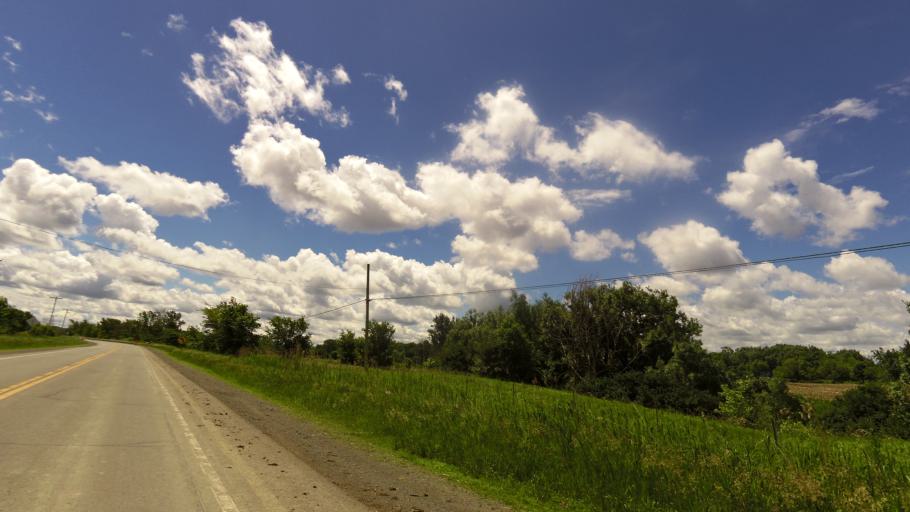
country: CA
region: Quebec
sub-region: Monteregie
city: Hudson
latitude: 45.5207
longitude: -74.1678
